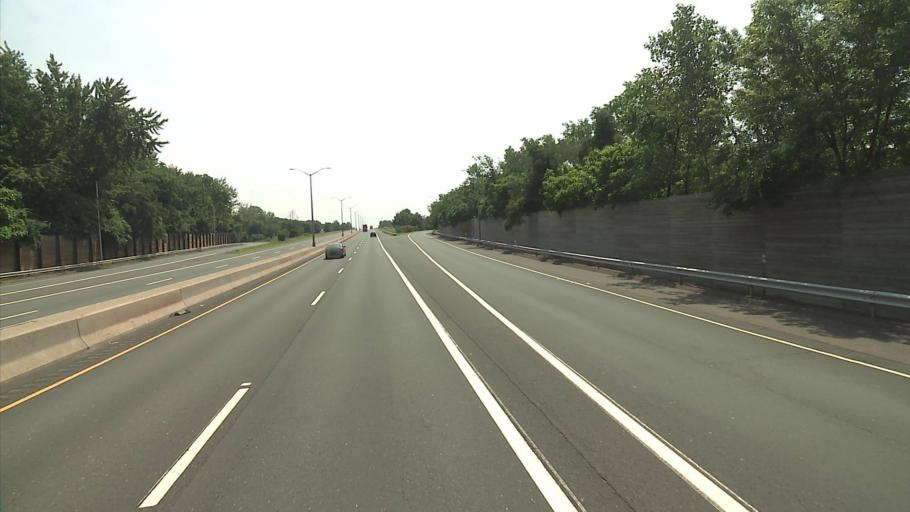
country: US
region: Connecticut
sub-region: Hartford County
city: South Windsor
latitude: 41.8068
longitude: -72.6204
